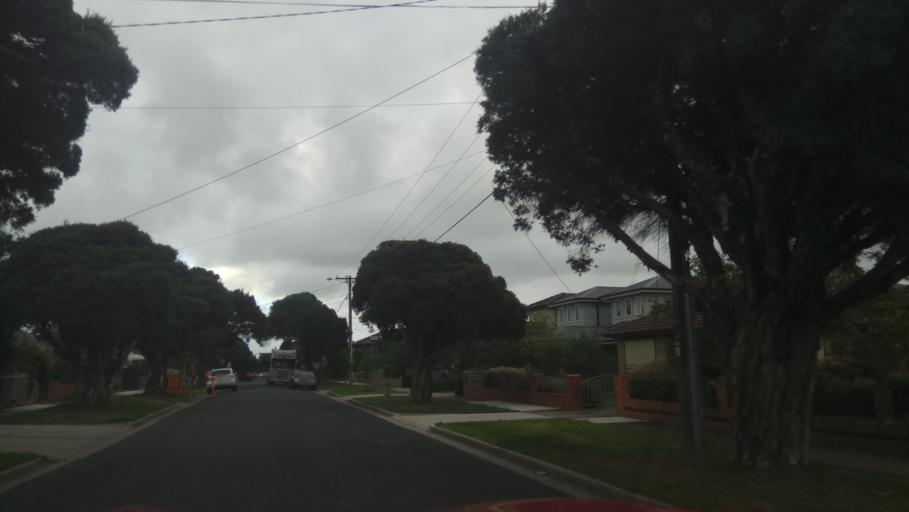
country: AU
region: Victoria
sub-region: Hobsons Bay
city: Altona North
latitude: -37.8271
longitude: 144.8428
